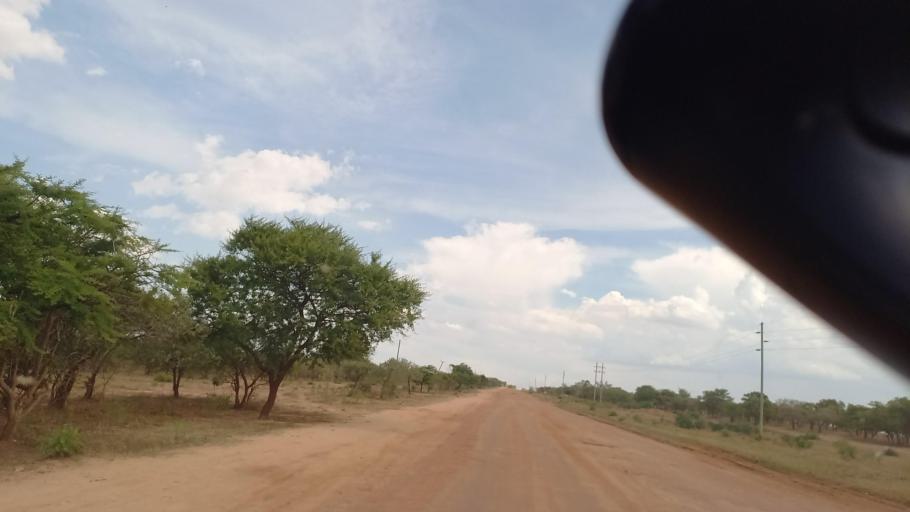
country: ZM
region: Lusaka
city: Kafue
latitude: -16.1413
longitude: 28.0534
